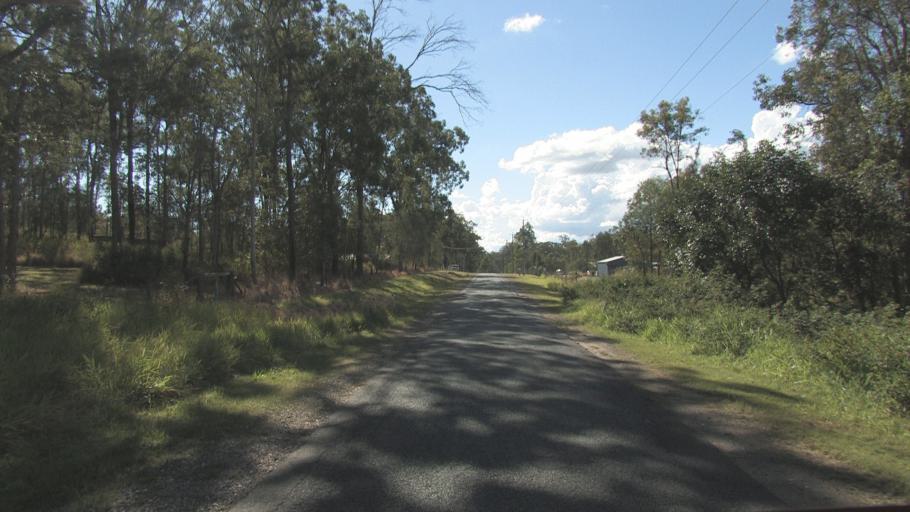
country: AU
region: Queensland
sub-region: Logan
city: Chambers Flat
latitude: -27.8073
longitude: 153.0824
